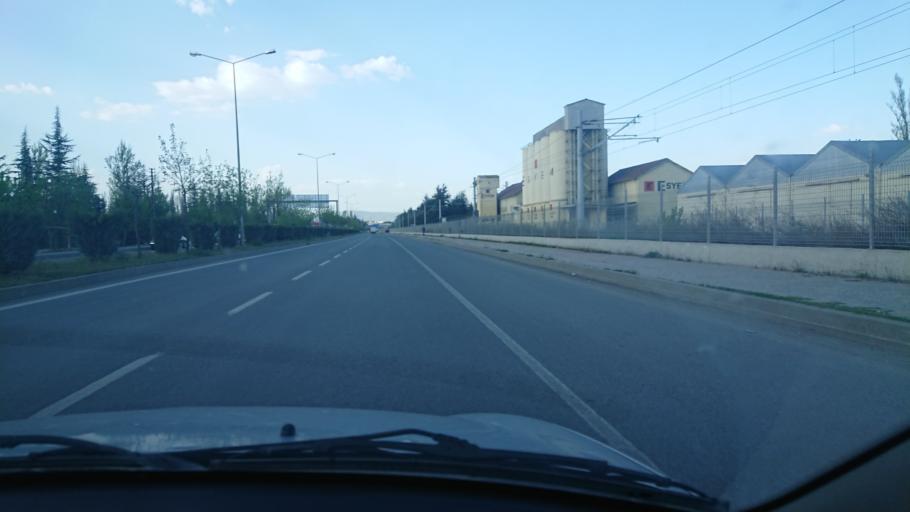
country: TR
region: Eskisehir
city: Eskisehir
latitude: 39.7603
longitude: 30.4772
